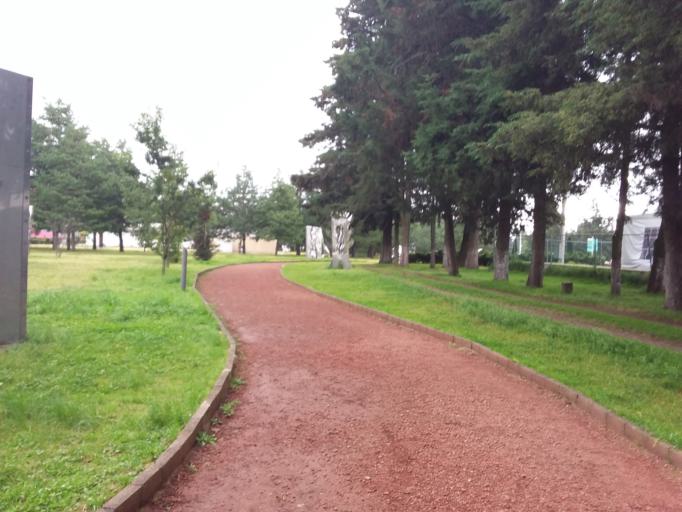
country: MX
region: Mexico
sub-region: Metepec
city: San Salvador Tizatlalli
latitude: 19.2492
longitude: -99.5801
